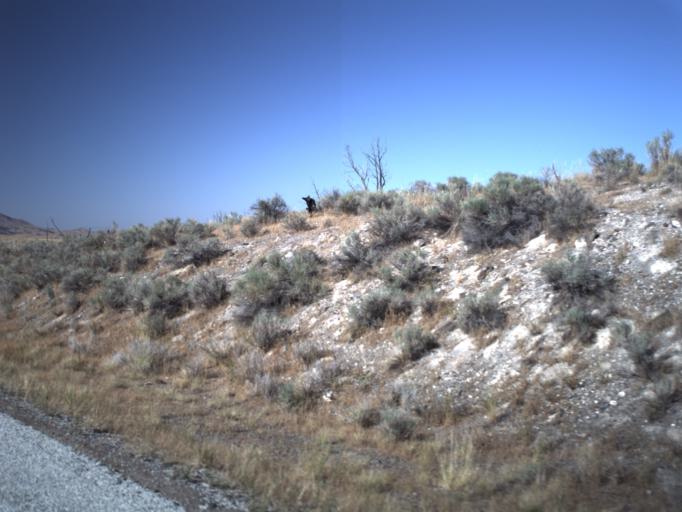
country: US
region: Utah
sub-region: Juab County
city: Mona
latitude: 39.7792
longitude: -112.1528
